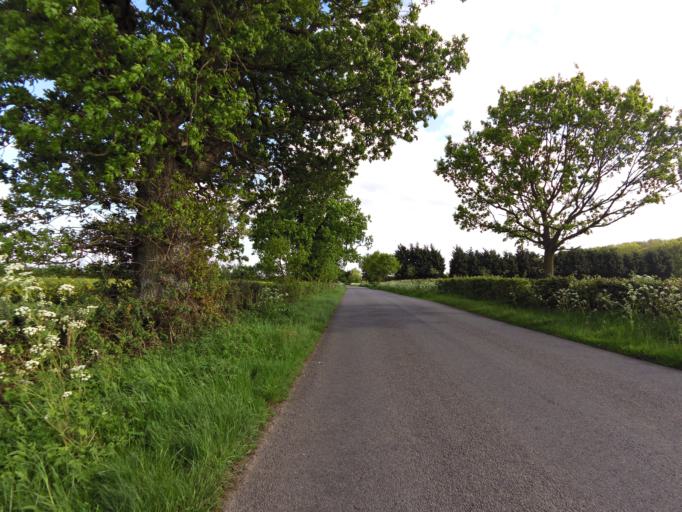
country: GB
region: England
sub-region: Suffolk
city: Beccles
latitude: 52.4328
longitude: 1.5423
